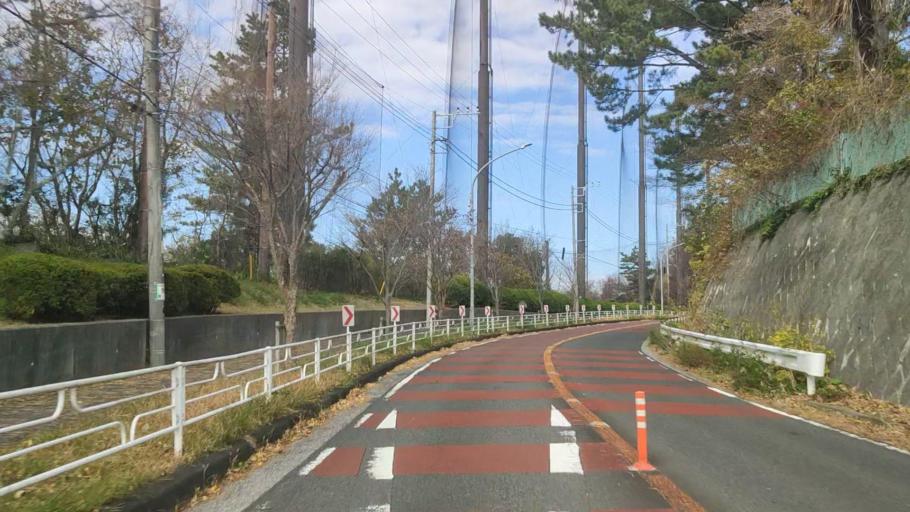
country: JP
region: Kanagawa
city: Minami-rinkan
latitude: 35.4449
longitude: 139.5380
